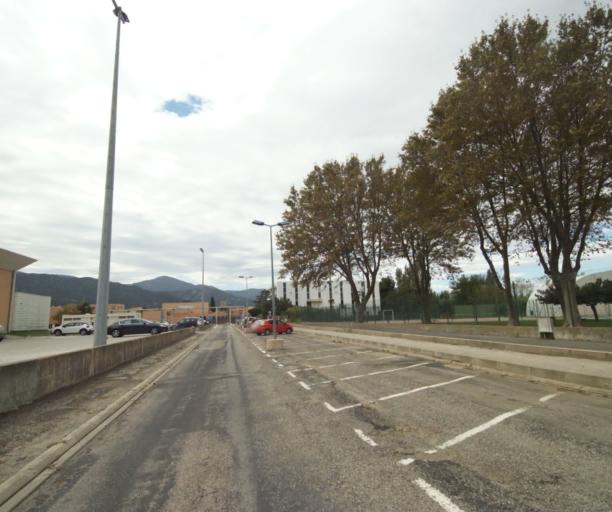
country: FR
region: Languedoc-Roussillon
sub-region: Departement des Pyrenees-Orientales
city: Argelers
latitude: 42.5509
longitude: 3.0301
